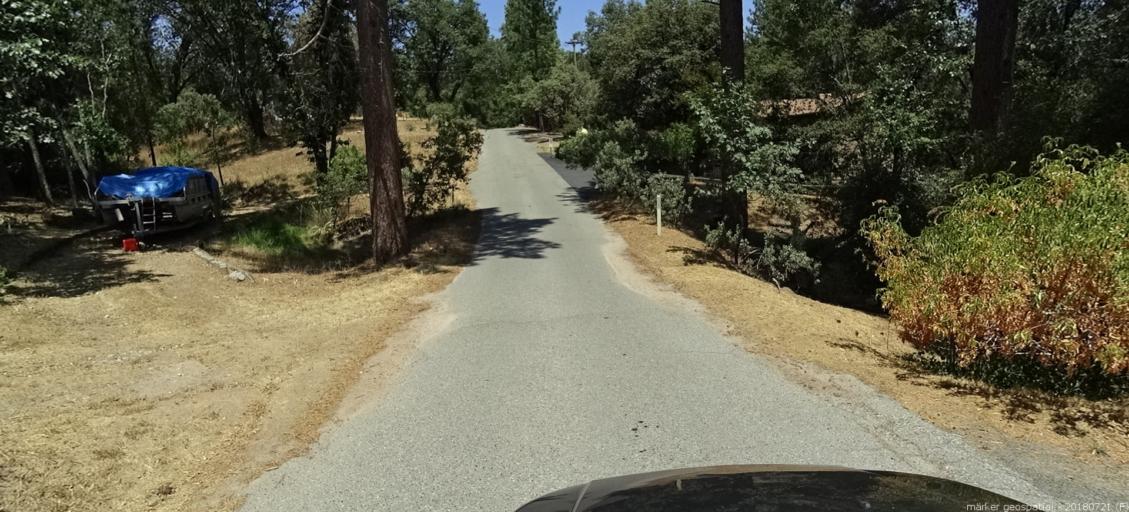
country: US
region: California
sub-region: Madera County
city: Oakhurst
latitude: 37.2692
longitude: -119.5354
